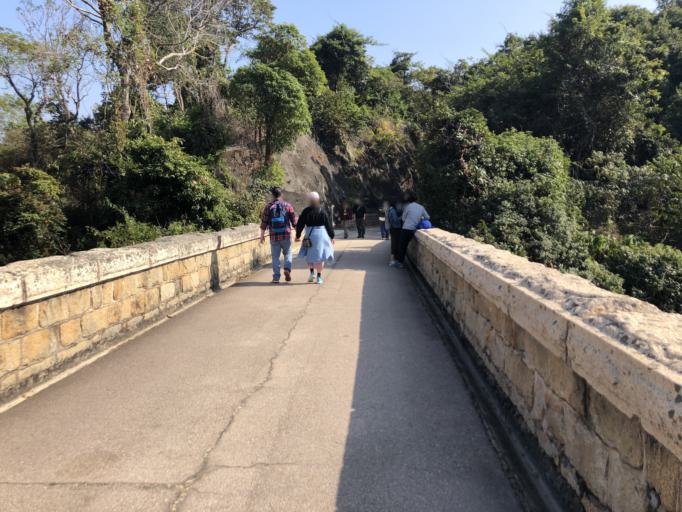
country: HK
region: Wanchai
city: Wan Chai
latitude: 22.2485
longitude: 114.2139
